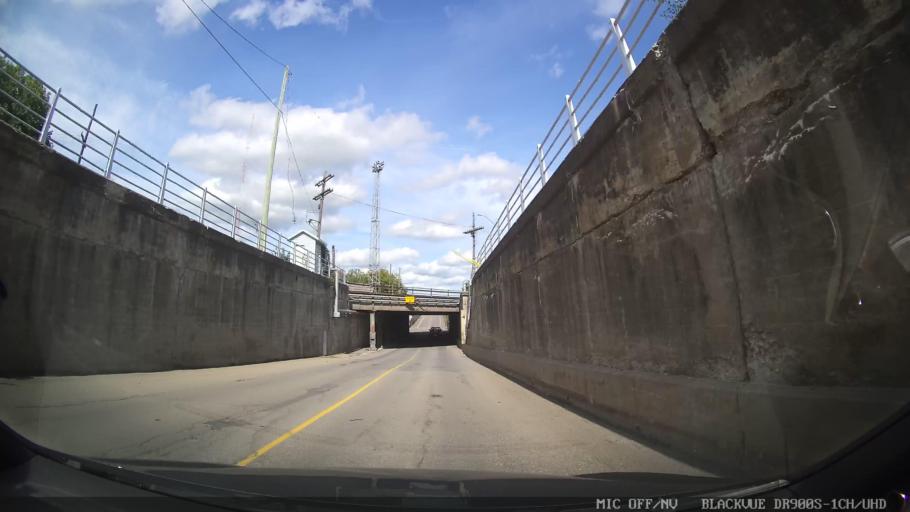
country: CA
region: Ontario
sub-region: Lanark County
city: Smiths Falls
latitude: 44.9035
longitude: -76.0101
